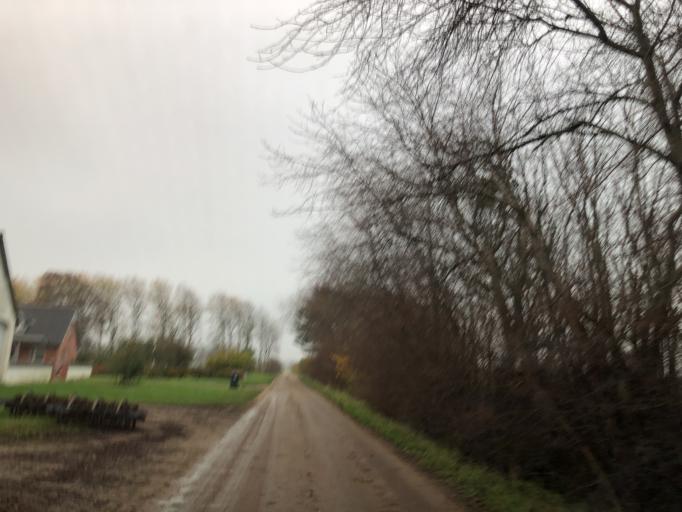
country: DK
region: Central Jutland
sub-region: Herning Kommune
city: Vildbjerg
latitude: 56.2126
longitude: 8.7270
